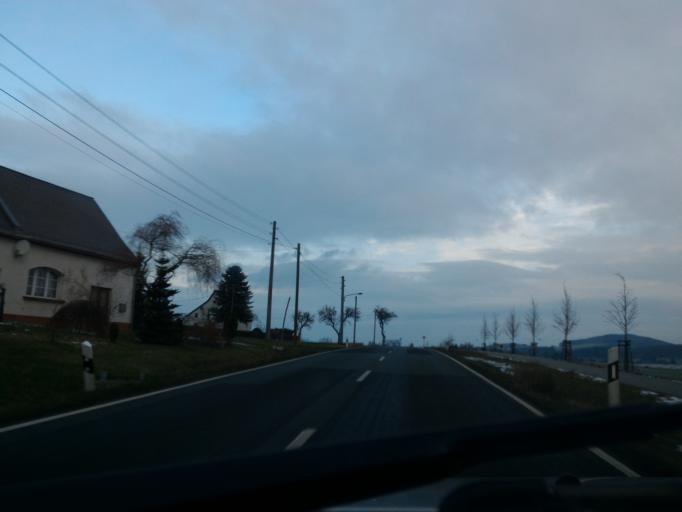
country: DE
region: Saxony
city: Leutersdorf
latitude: 50.9362
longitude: 14.6682
